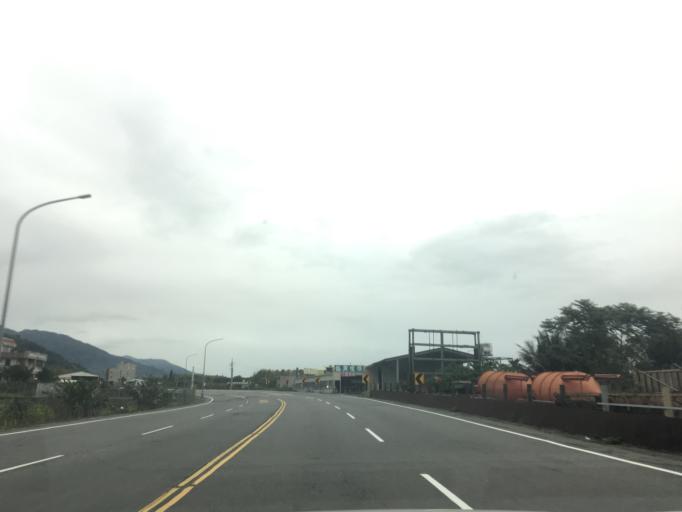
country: TW
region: Taiwan
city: Taitung City
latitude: 22.7260
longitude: 121.0560
